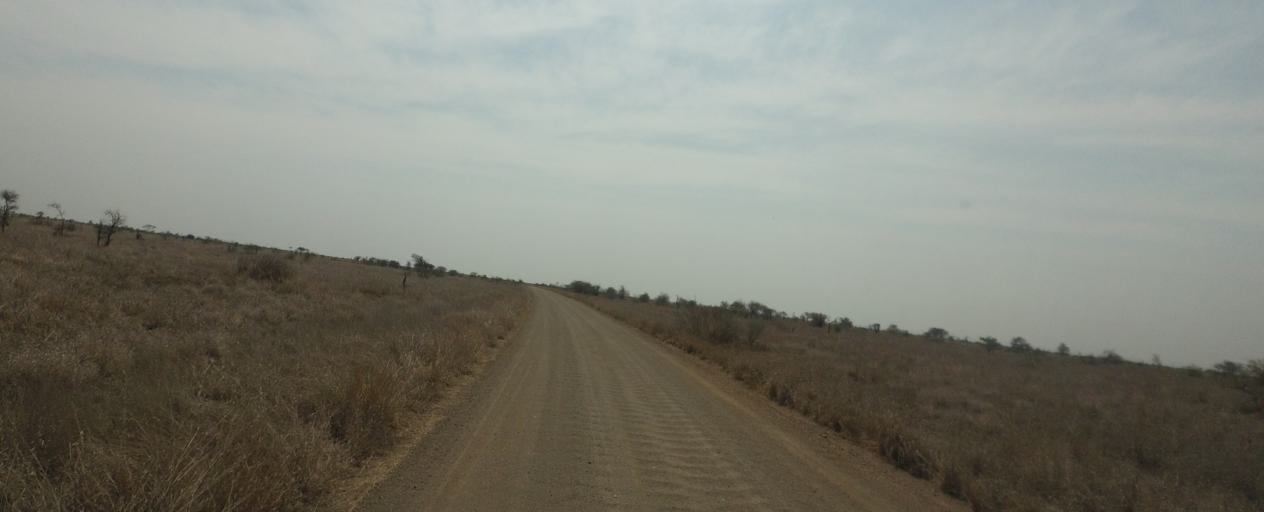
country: ZA
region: Limpopo
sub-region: Mopani District Municipality
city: Phalaborwa
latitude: -24.2609
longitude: 31.6841
